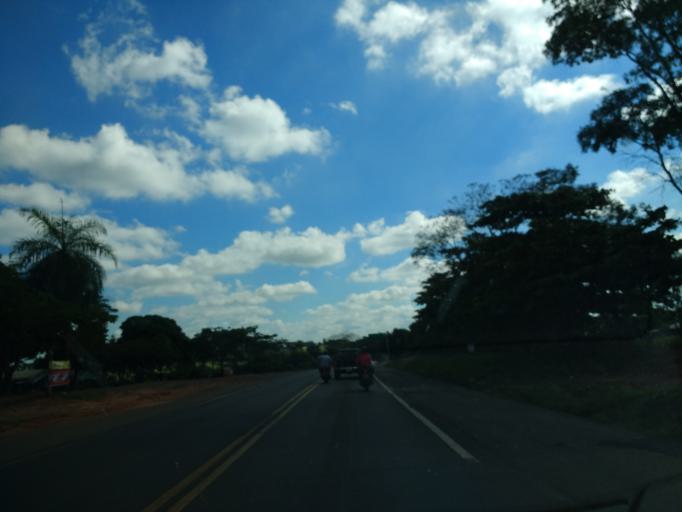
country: BR
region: Parana
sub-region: Alto Piquiri
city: Alto Piquiri
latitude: -23.8928
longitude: -53.4530
